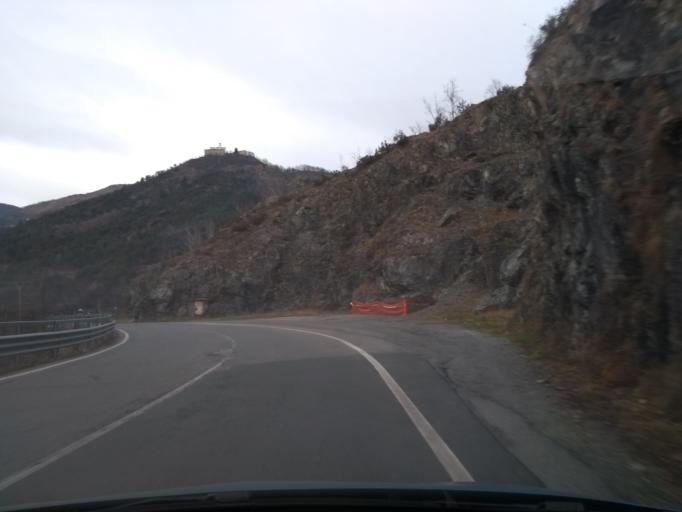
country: IT
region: Piedmont
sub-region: Provincia di Torino
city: La Villa
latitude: 45.2664
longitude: 7.4413
